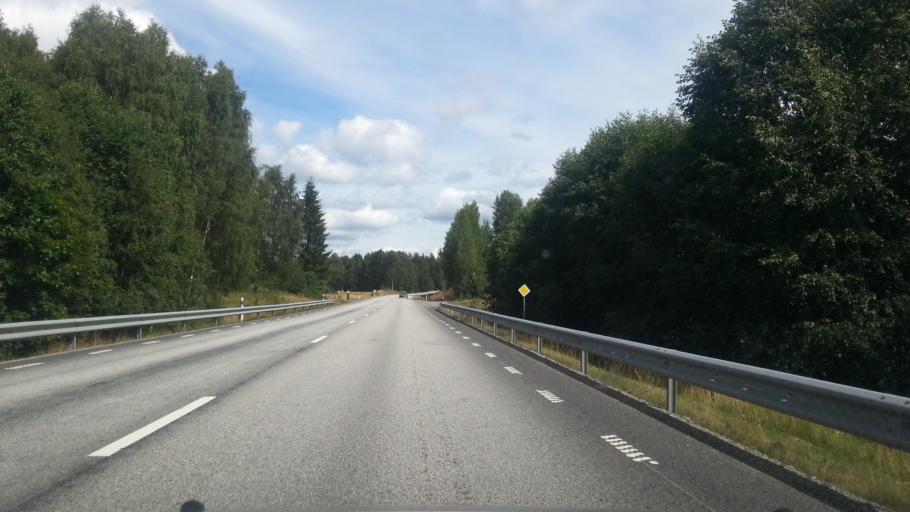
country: SE
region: OErebro
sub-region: Lindesbergs Kommun
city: Lindesberg
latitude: 59.6862
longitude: 15.3298
